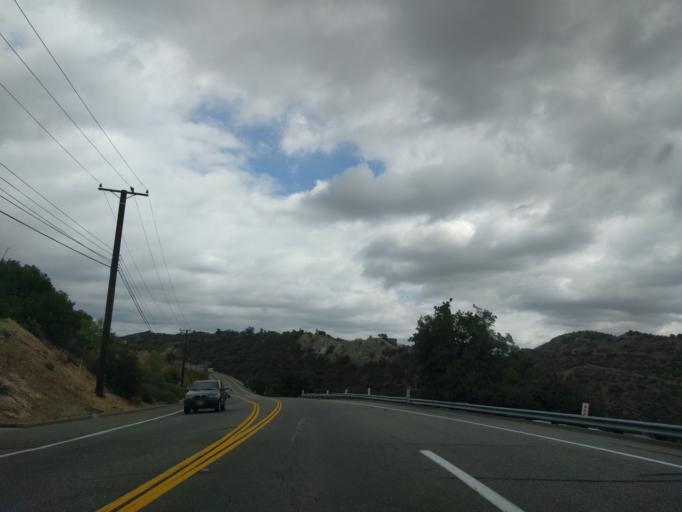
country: US
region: California
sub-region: Orange County
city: Foothill Ranch
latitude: 33.7023
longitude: -117.6418
